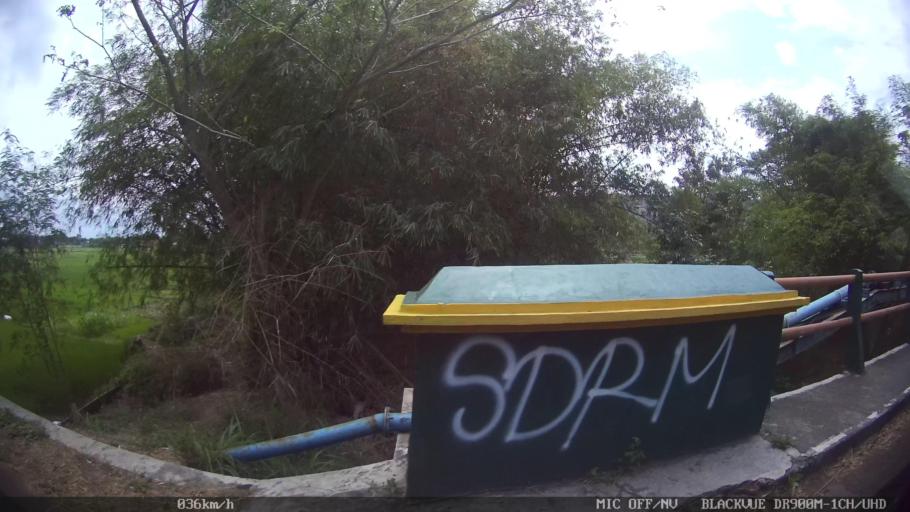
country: ID
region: Central Java
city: Candi Prambanan
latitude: -7.8109
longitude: 110.5036
